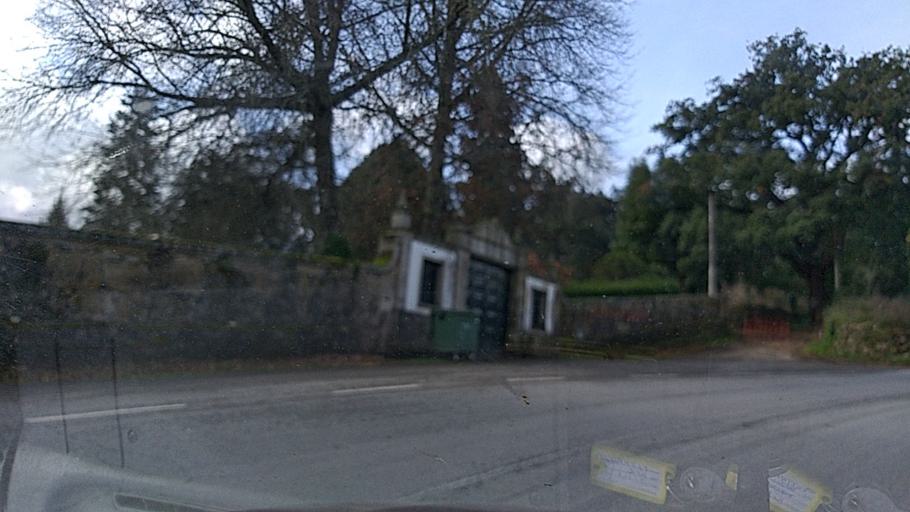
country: PT
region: Viseu
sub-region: Satao
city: Satao
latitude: 40.6708
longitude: -7.6967
